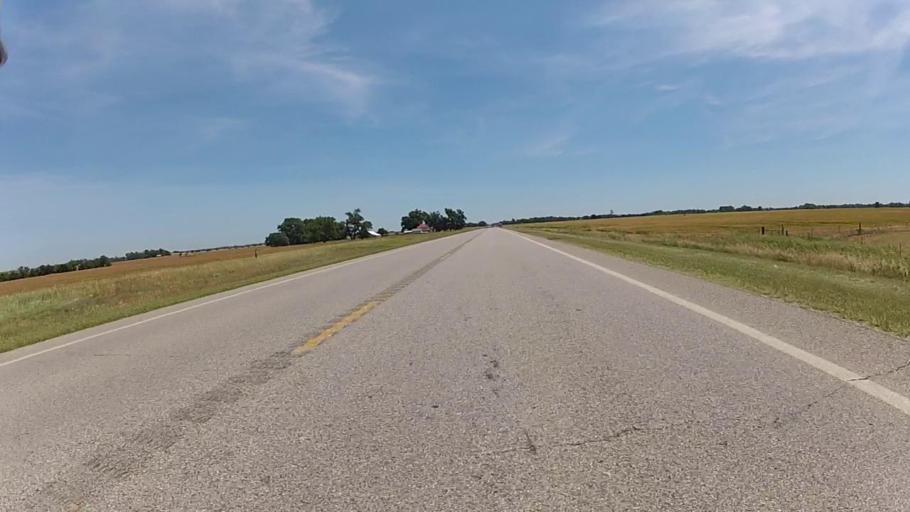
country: US
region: Kansas
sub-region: Barber County
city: Medicine Lodge
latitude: 37.2534
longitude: -98.4501
